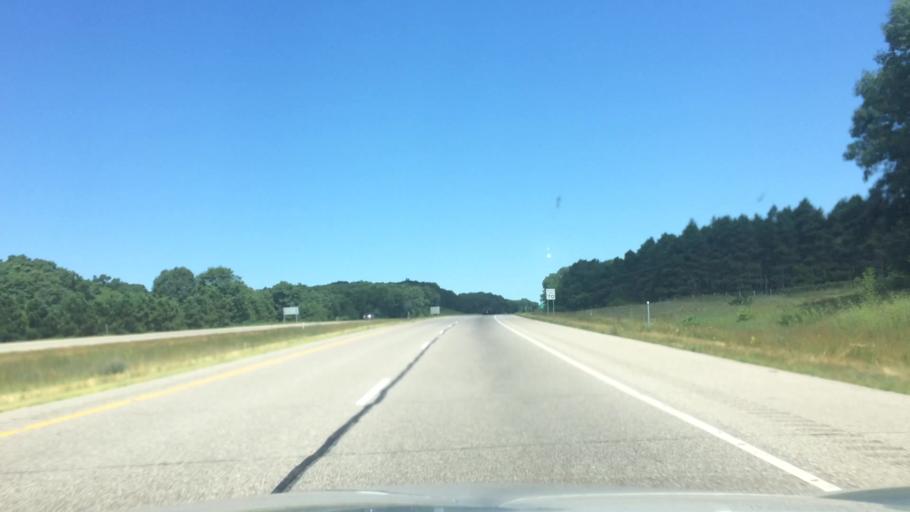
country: US
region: Wisconsin
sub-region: Marquette County
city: Westfield
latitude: 44.0431
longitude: -89.5360
